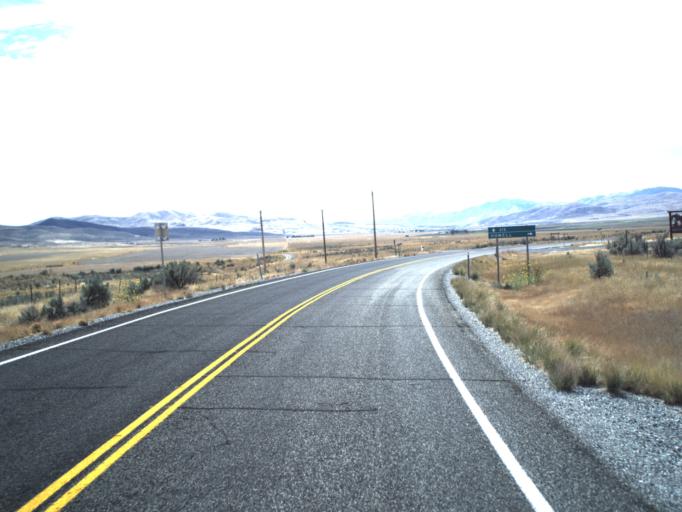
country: US
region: Utah
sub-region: Box Elder County
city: Garland
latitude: 41.7968
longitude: -112.4163
